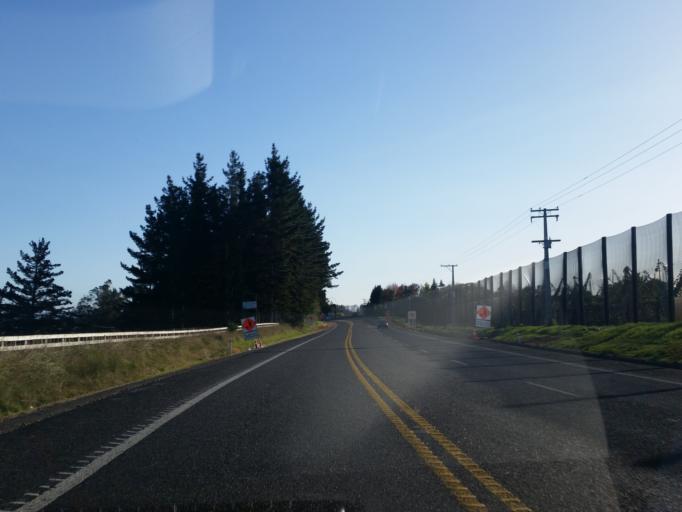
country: NZ
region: Bay of Plenty
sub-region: Western Bay of Plenty District
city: Katikati
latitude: -37.6201
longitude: 175.9511
